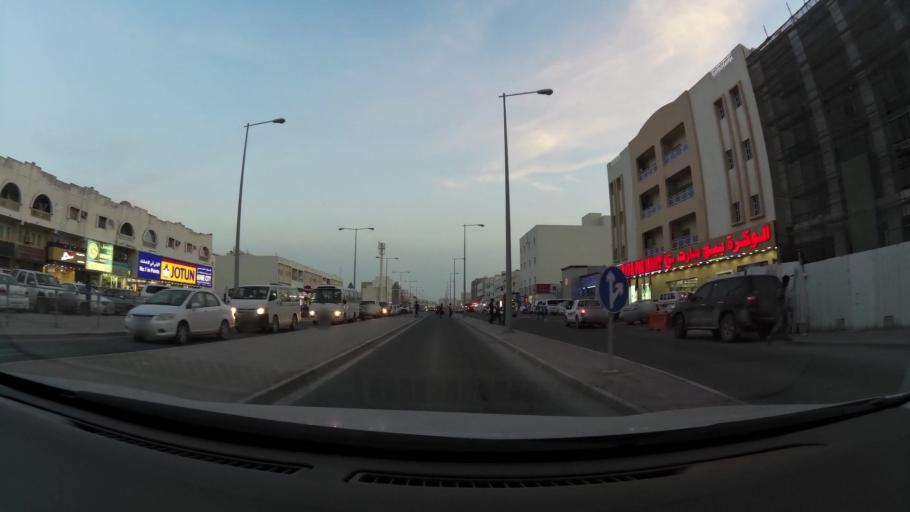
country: QA
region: Al Wakrah
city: Al Wakrah
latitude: 25.1604
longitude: 51.5987
